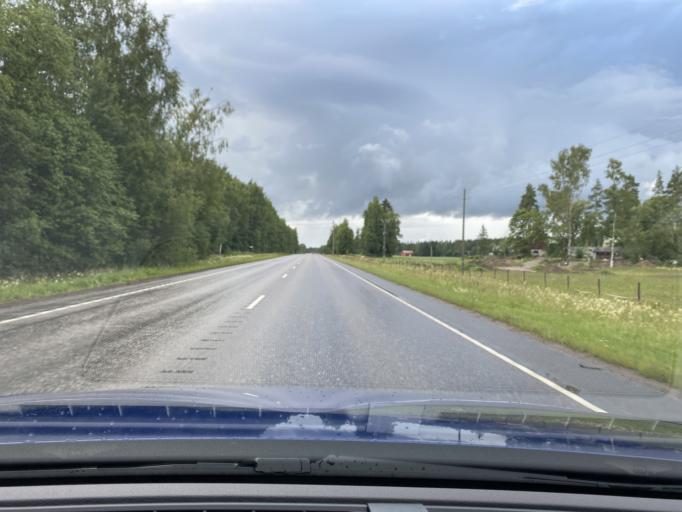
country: FI
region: Uusimaa
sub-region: Helsinki
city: Nurmijaervi
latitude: 60.5452
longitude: 24.8309
